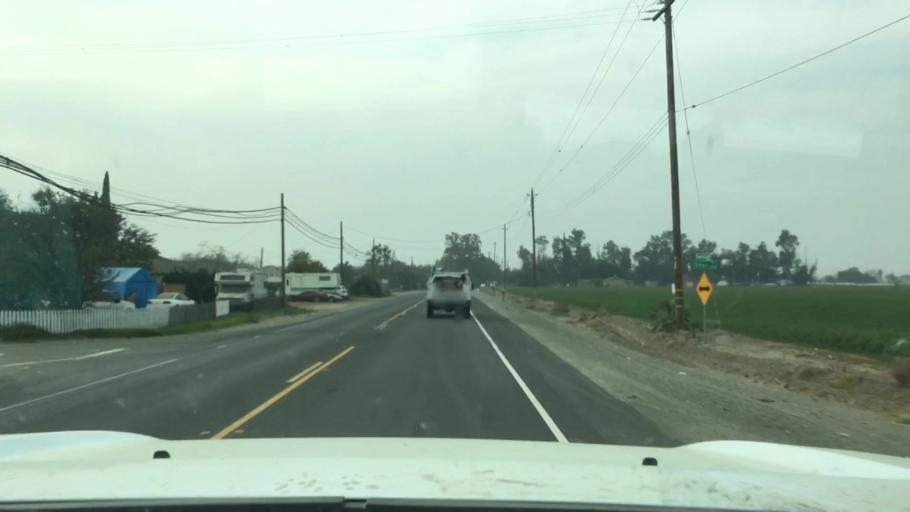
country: US
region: California
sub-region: San Joaquin County
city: French Camp
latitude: 37.8700
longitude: -121.2470
